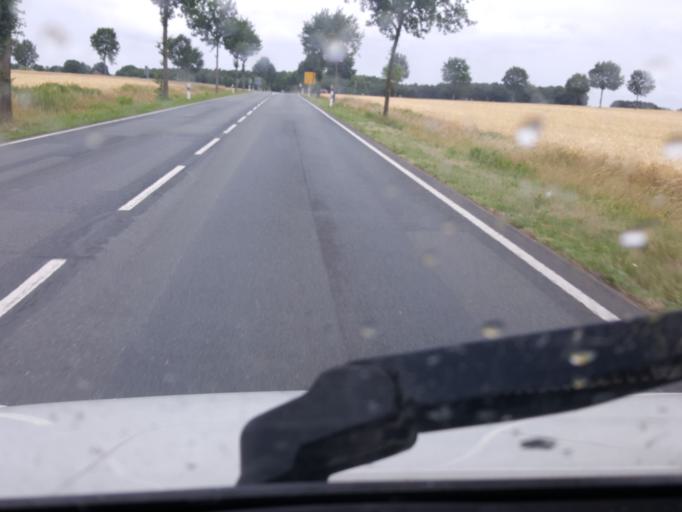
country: DE
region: Lower Saxony
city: Raddestorf
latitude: 52.4357
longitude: 8.9407
